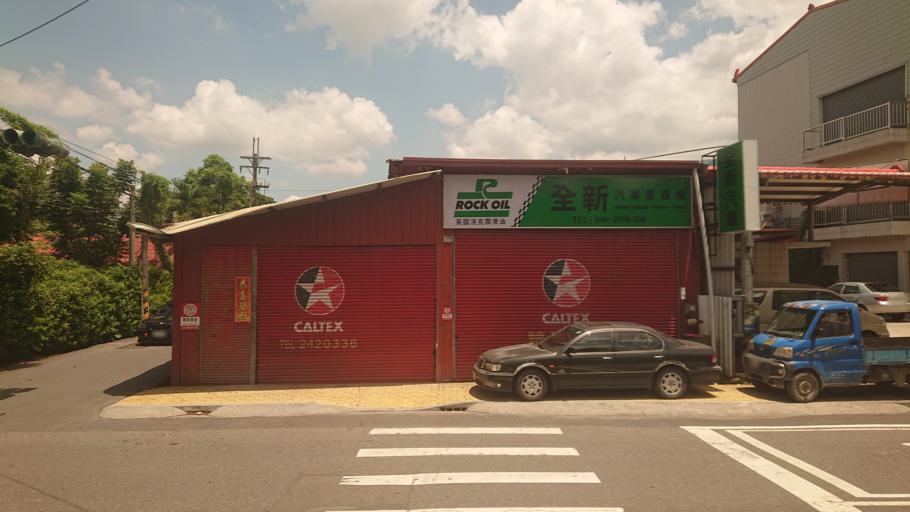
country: TW
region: Taiwan
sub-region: Nantou
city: Puli
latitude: 23.9742
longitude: 120.9785
